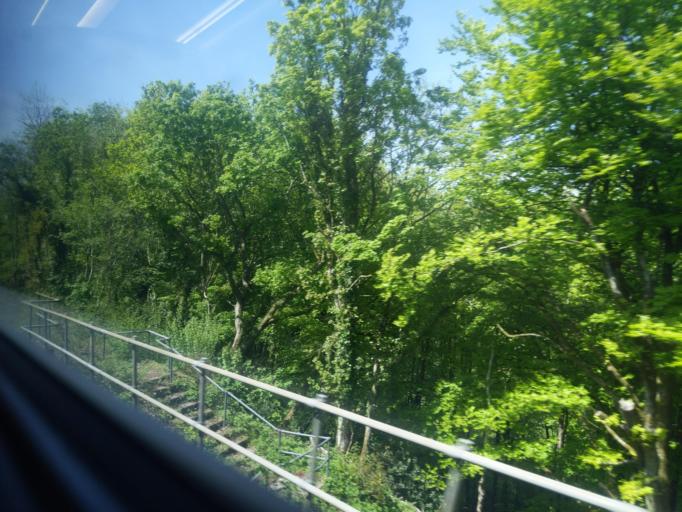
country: GB
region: England
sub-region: Cornwall
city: Liskeard
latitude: 50.4529
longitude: -4.5695
